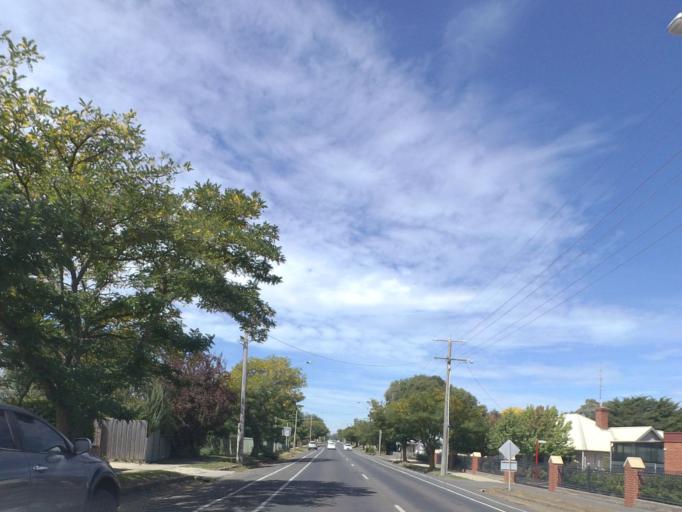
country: AU
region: Victoria
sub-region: Mount Alexander
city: Castlemaine
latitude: -37.2524
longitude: 144.4592
